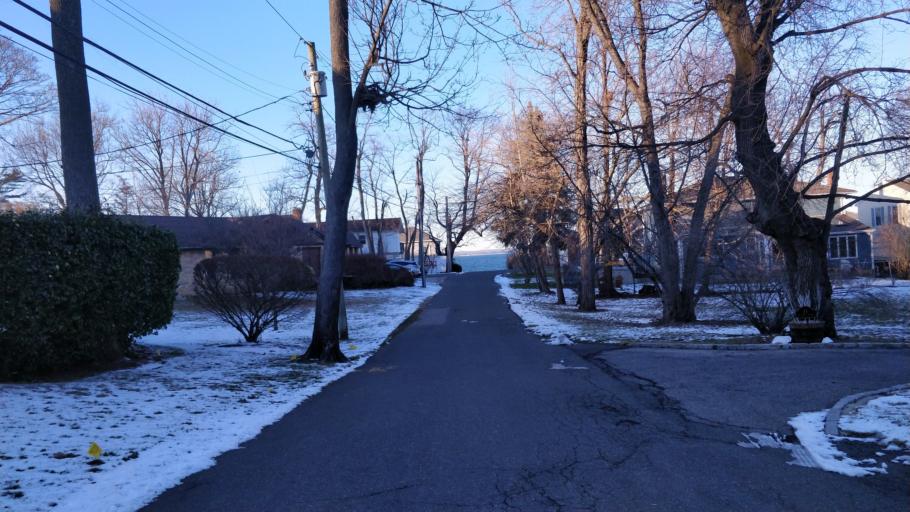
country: US
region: New York
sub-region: Nassau County
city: Bayville
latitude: 40.9140
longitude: -73.5698
